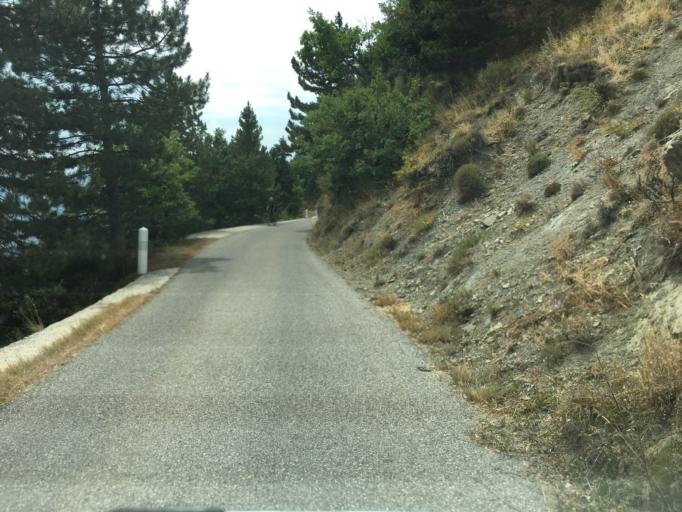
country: FR
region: Provence-Alpes-Cote d'Azur
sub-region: Departement des Alpes-de-Haute-Provence
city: Digne-les-Bains
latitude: 44.1993
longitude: 6.1459
